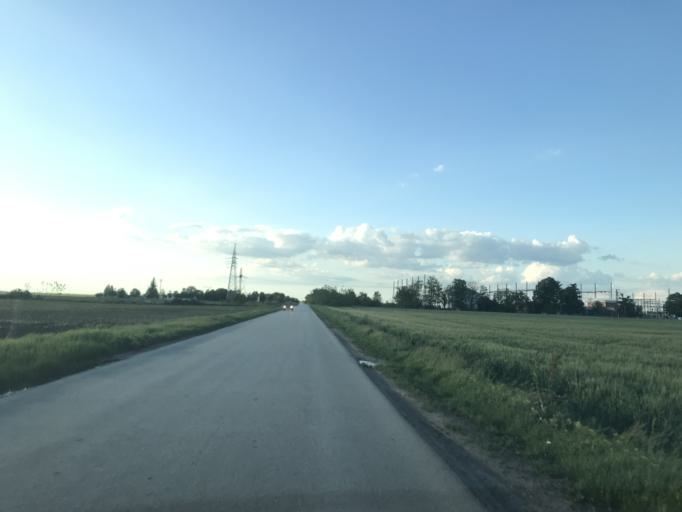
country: RS
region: Autonomna Pokrajina Vojvodina
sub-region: Srednjebanatski Okrug
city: Zrenjanin
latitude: 45.4103
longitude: 20.3928
